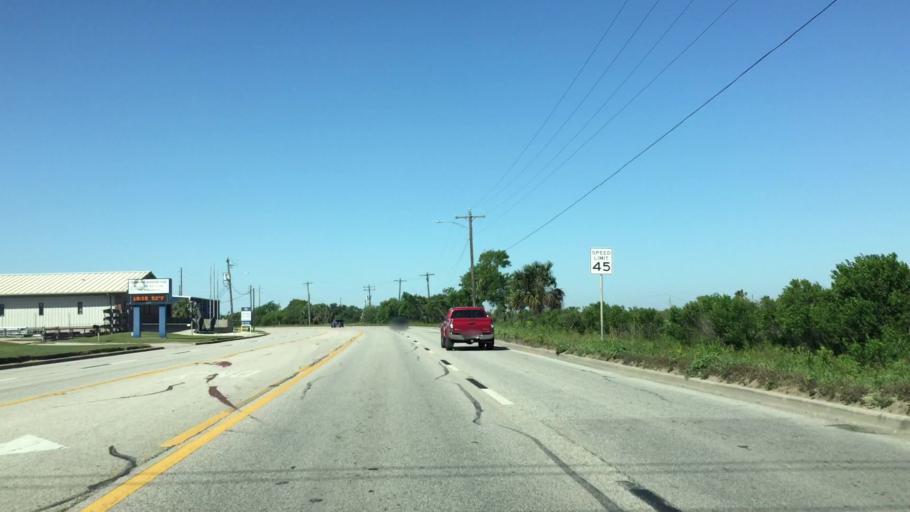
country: US
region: Texas
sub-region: Galveston County
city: Galveston
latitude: 29.2922
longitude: -94.8600
